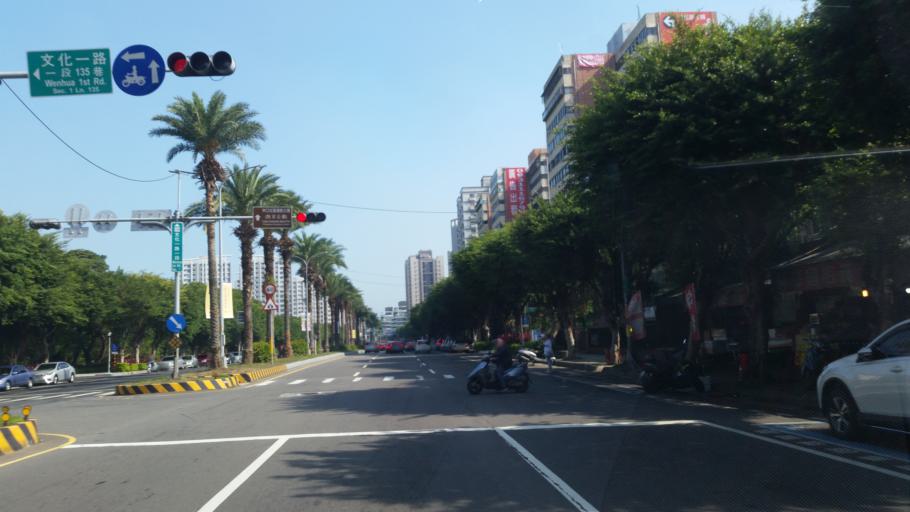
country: TW
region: Taiwan
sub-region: Taoyuan
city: Taoyuan
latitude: 25.0715
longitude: 121.3739
